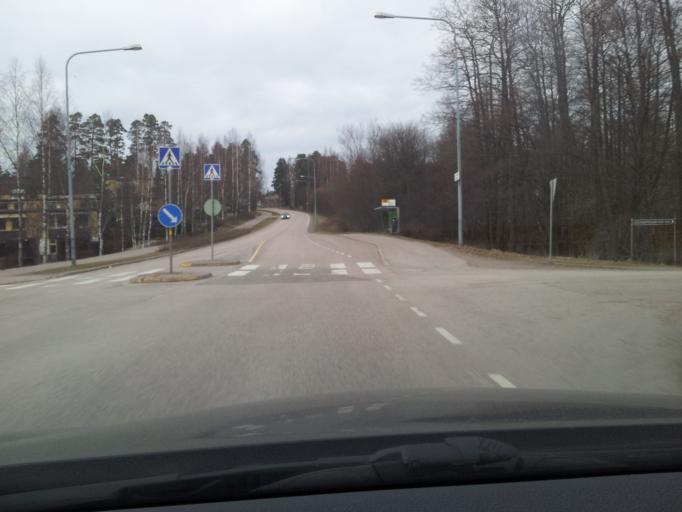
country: FI
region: Uusimaa
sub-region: Helsinki
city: Espoo
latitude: 60.1415
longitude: 24.6568
